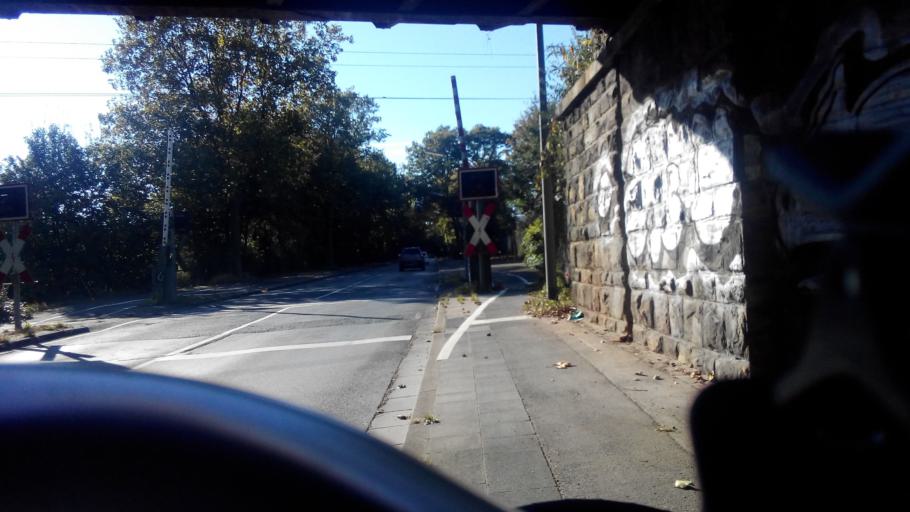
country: DE
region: North Rhine-Westphalia
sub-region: Regierungsbezirk Munster
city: Gelsenkirchen
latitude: 51.5118
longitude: 7.1368
